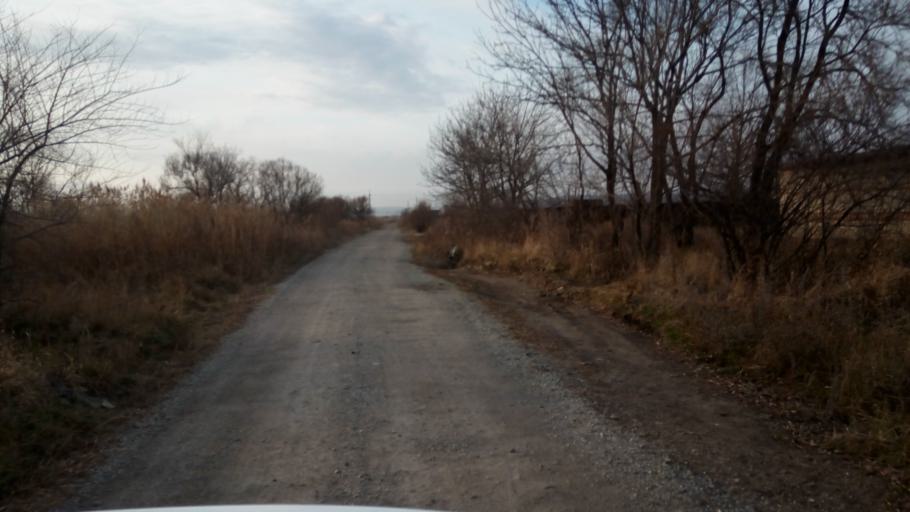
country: RU
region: Primorskiy
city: Ussuriysk
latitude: 43.7994
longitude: 131.9514
